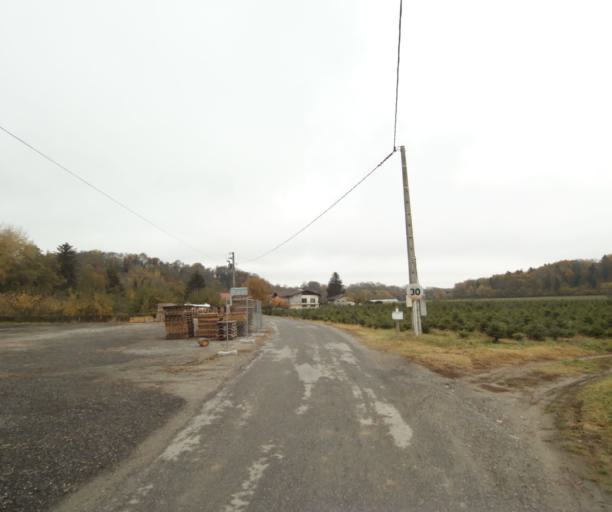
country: FR
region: Rhone-Alpes
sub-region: Departement de la Haute-Savoie
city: Arthaz-Pont-Notre-Dame
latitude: 46.1503
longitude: 6.2727
